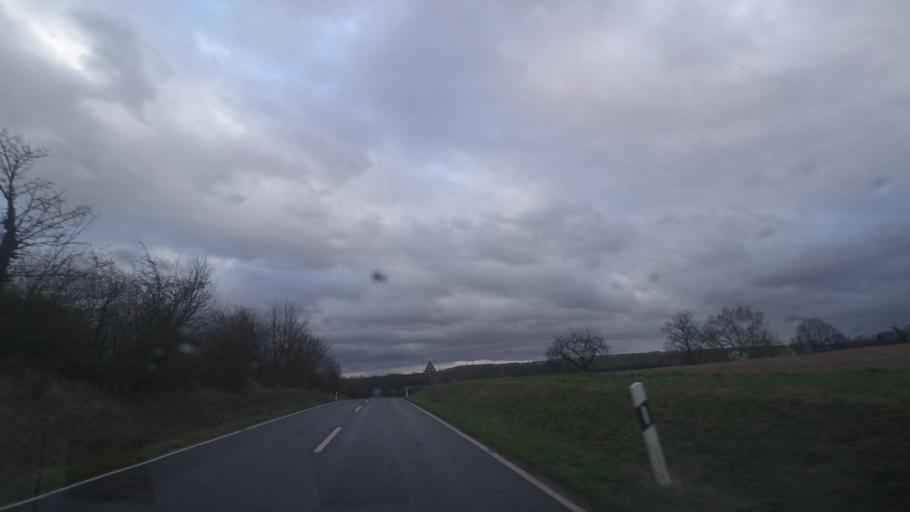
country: DE
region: Rheinland-Pfalz
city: Eppelsheim
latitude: 49.7015
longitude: 8.1702
